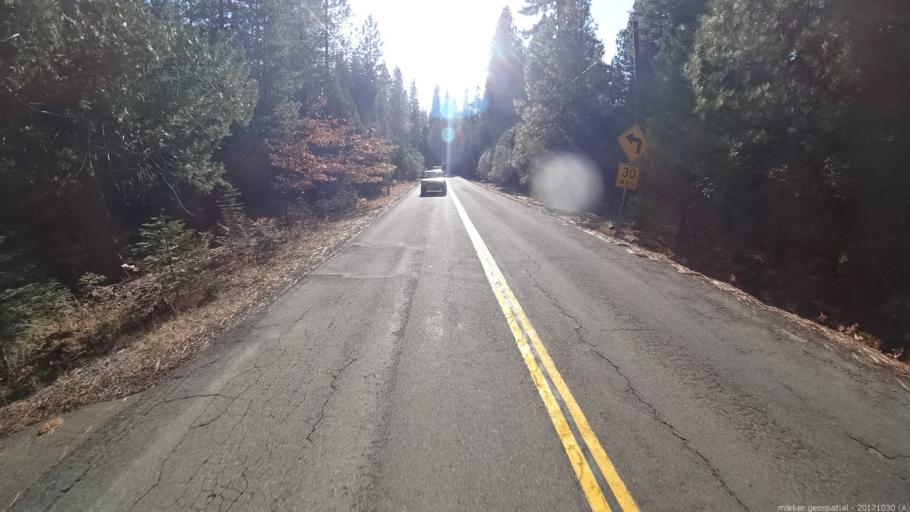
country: US
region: California
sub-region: Shasta County
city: Shingletown
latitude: 40.5295
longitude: -121.7459
